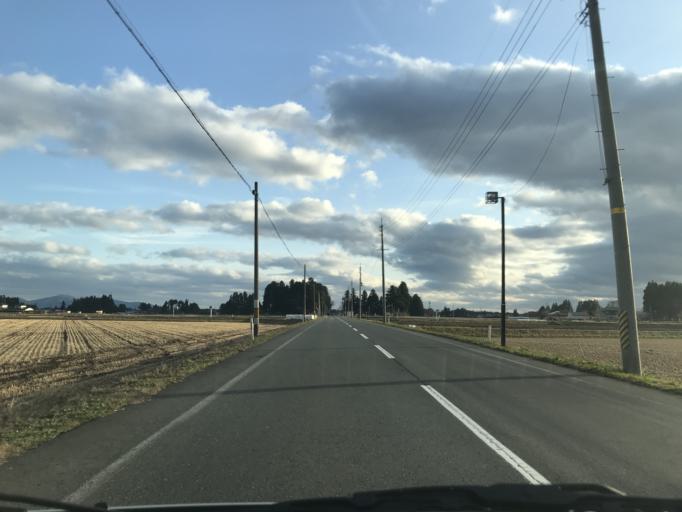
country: JP
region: Iwate
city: Mizusawa
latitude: 39.1427
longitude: 141.0496
